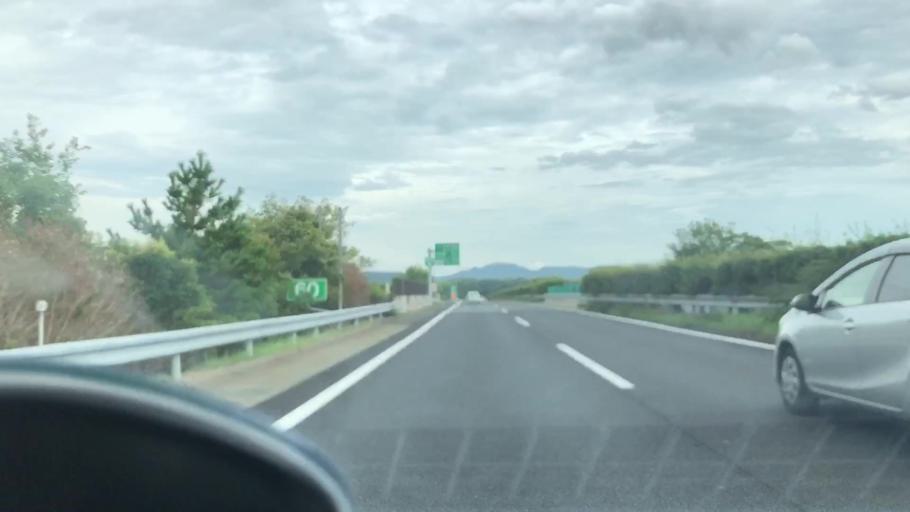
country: JP
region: Hyogo
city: Yashiro
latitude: 34.9299
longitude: 134.9588
